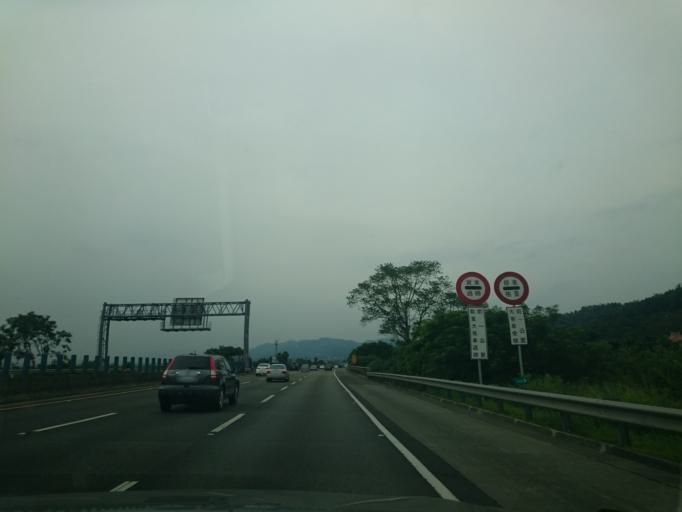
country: TW
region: Taiwan
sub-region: Nantou
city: Nantou
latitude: 23.8623
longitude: 120.7027
